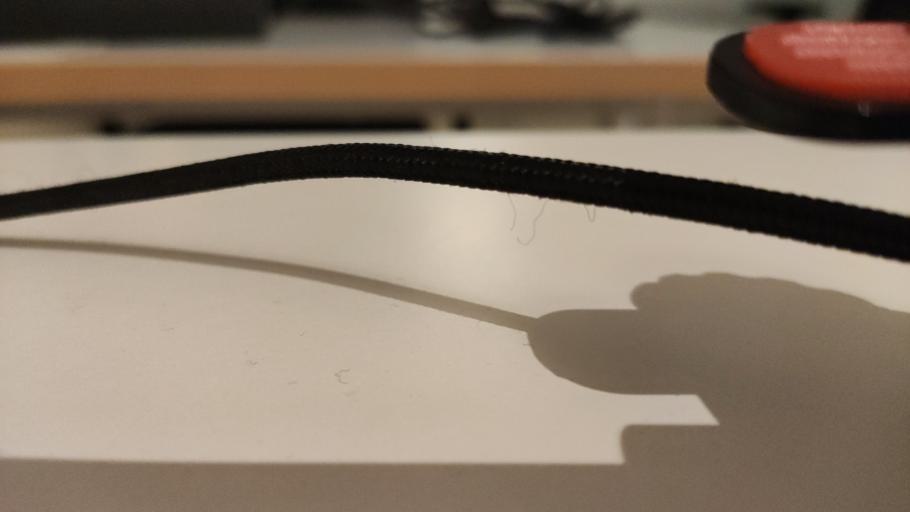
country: RU
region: Moskovskaya
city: Il'inskiy Pogost
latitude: 55.4945
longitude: 38.8747
